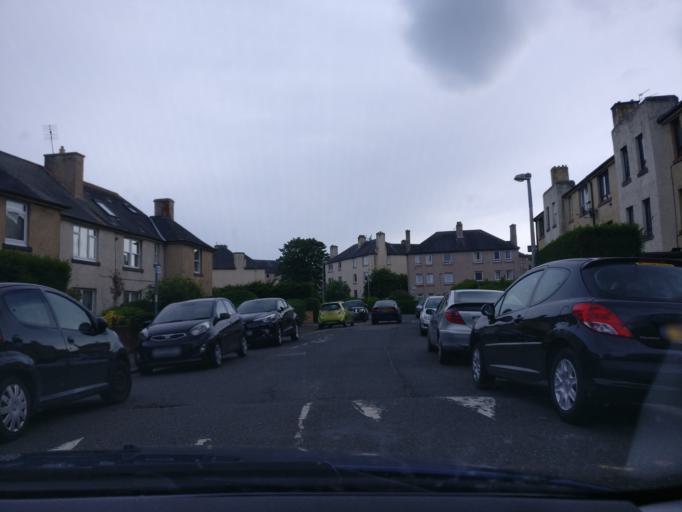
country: GB
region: Scotland
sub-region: West Lothian
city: Seafield
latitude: 55.9599
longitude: -3.1397
